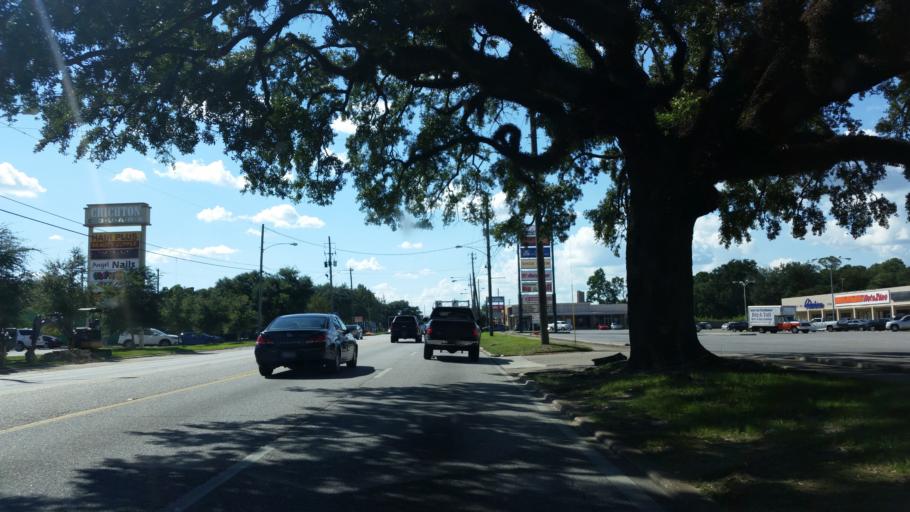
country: US
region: Alabama
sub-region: Mobile County
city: Prichard
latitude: 30.6997
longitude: -88.1108
